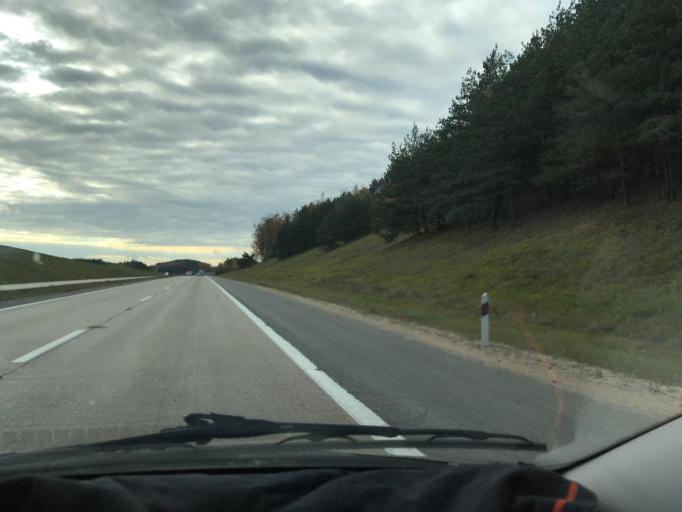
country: BY
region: Minsk
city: Astrashytski Haradok
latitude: 54.0729
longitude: 27.7297
